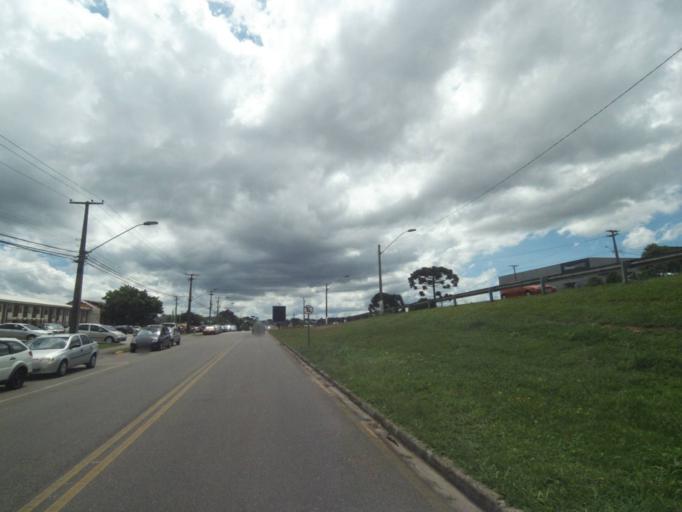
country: BR
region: Parana
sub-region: Curitiba
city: Curitiba
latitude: -25.4309
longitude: -49.3310
